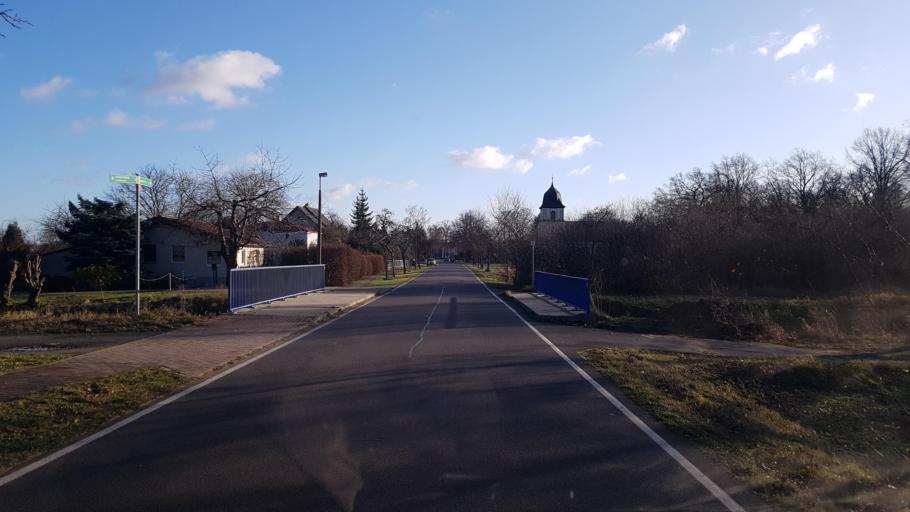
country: DE
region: Brandenburg
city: Forst
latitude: 51.7683
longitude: 14.5913
